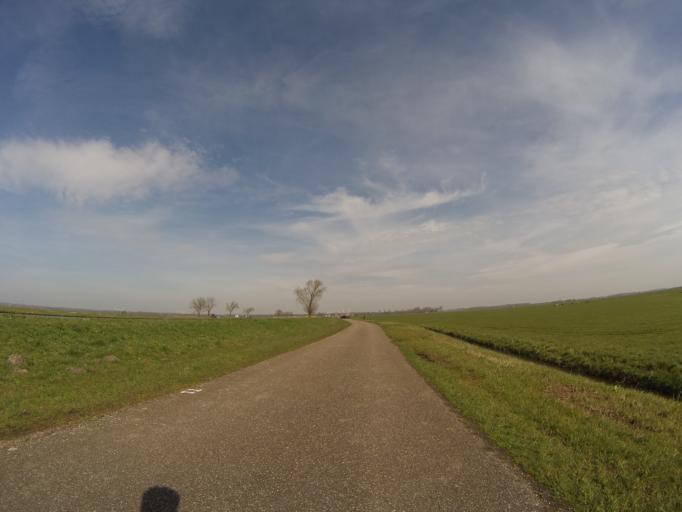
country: NL
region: Gelderland
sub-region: Gemeente Nijkerk
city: Nijkerk
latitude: 52.2428
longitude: 5.4711
